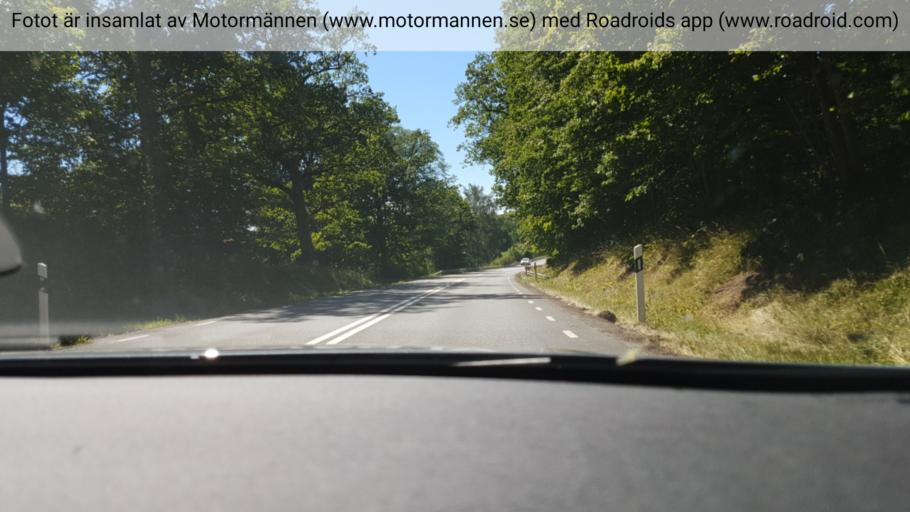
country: SE
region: Joenkoeping
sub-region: Jonkopings Kommun
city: Graenna
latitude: 58.0018
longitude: 14.5089
